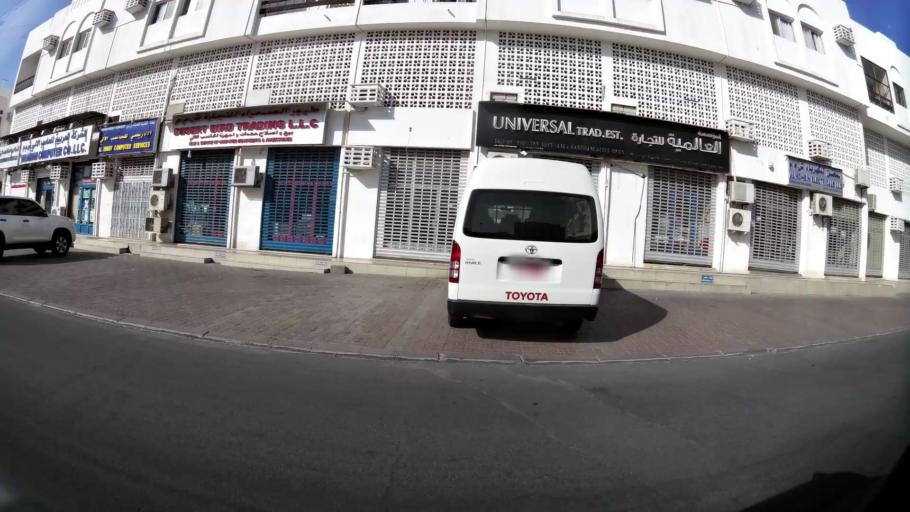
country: OM
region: Muhafazat Masqat
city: Muscat
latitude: 23.5926
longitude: 58.5484
